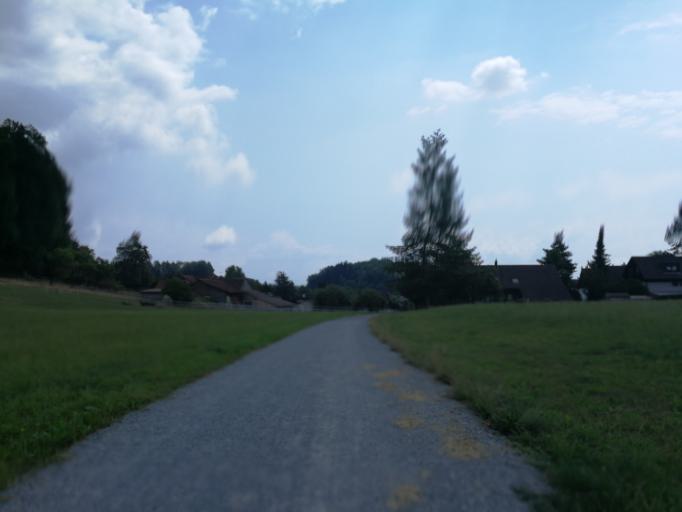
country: CH
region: Zurich
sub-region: Bezirk Hinwil
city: Gossau
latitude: 47.3256
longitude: 8.7578
